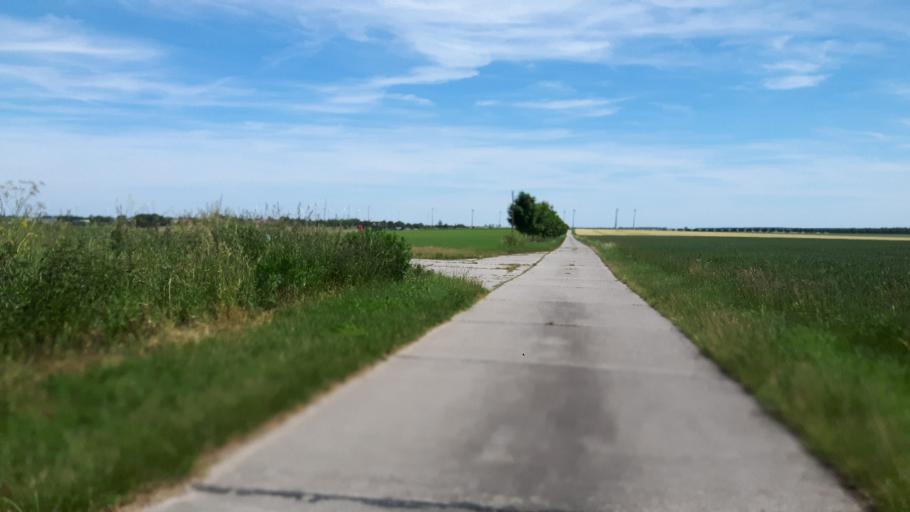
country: DE
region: Saxony-Anhalt
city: Kropstadt
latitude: 52.0014
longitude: 12.7545
